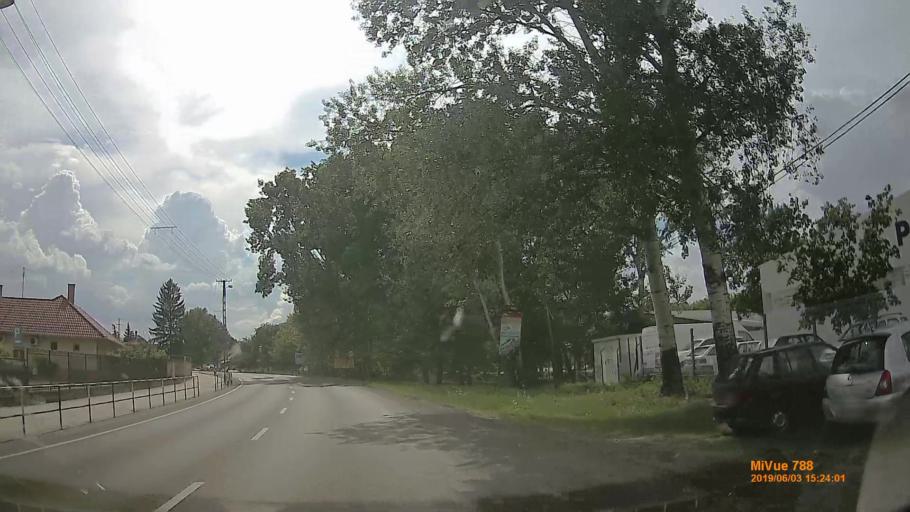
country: HU
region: Bacs-Kiskun
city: Tazlar
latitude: 46.6175
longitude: 19.4807
